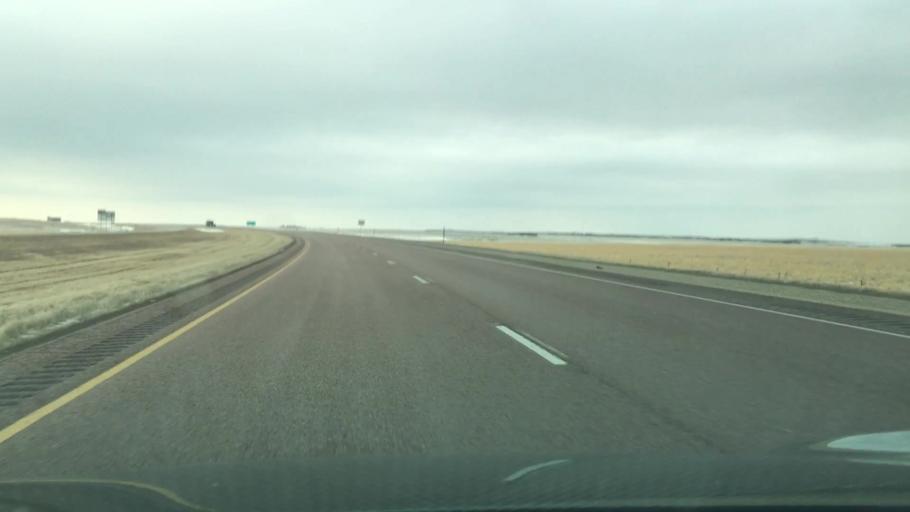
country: US
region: South Dakota
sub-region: Lyman County
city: Kennebec
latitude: 43.8679
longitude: -99.6161
